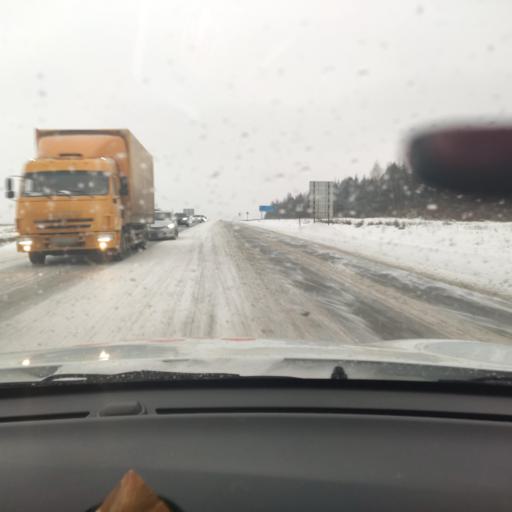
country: RU
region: Tatarstan
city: Sviyazhsk
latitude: 55.7325
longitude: 48.7977
